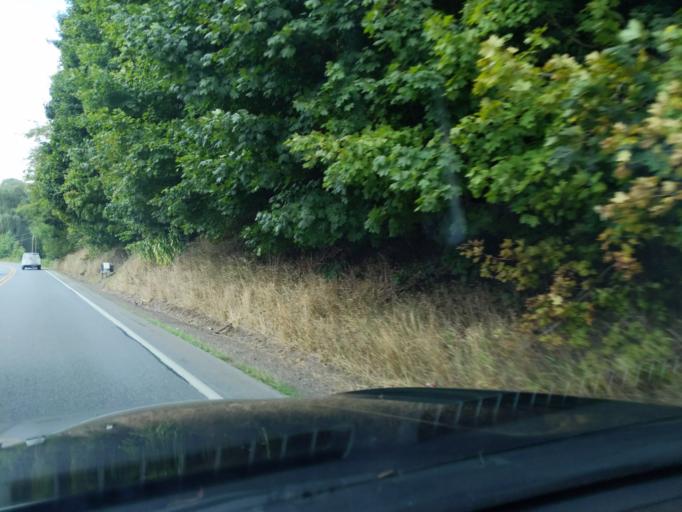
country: US
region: Pennsylvania
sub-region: Blair County
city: Duncansville
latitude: 40.3796
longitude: -78.4181
